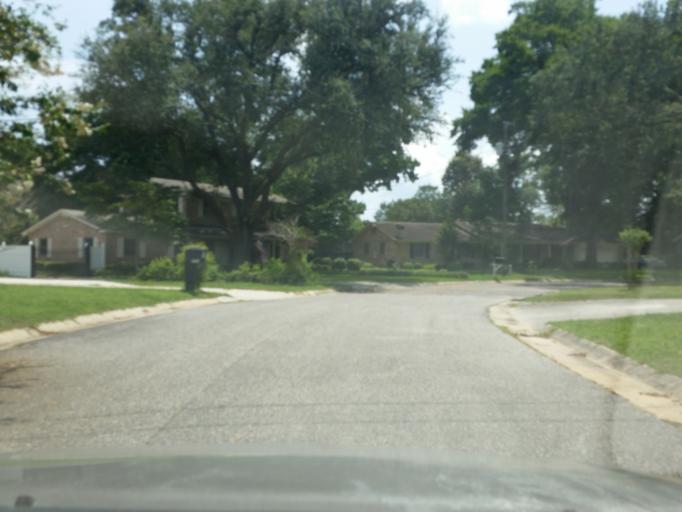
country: US
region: Florida
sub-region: Escambia County
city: Ferry Pass
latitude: 30.5112
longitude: -87.1909
